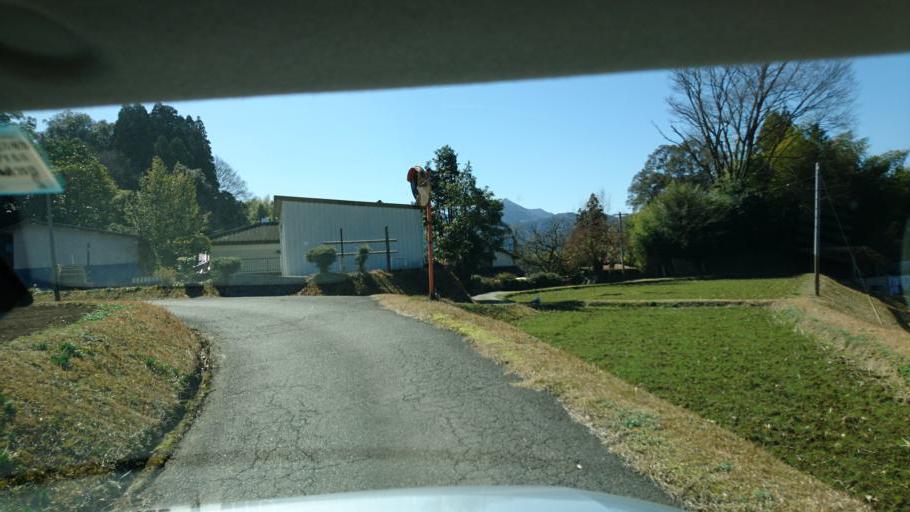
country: JP
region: Oita
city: Takedamachi
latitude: 32.7193
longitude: 131.3056
